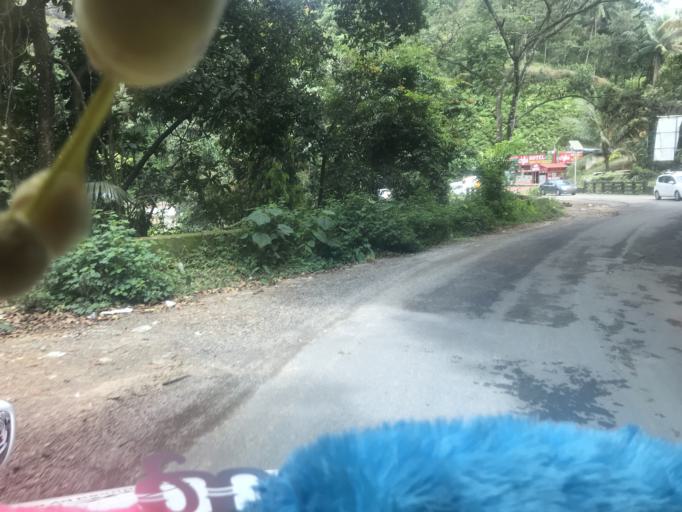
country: IN
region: Kerala
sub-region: Idukki
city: Kuttampuzha
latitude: 10.0461
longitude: 76.8396
